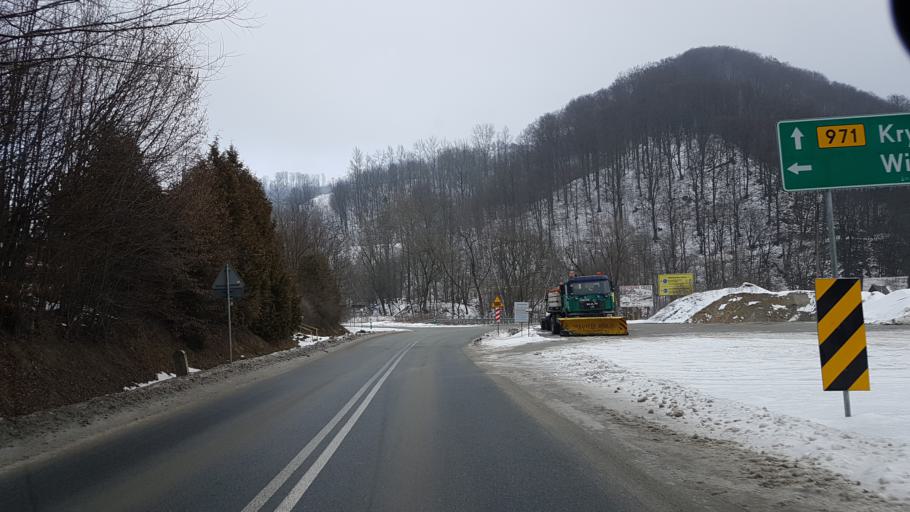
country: PL
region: Lesser Poland Voivodeship
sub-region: Powiat nowosadecki
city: Piwniczna-Zdroj
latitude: 49.4031
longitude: 20.7529
